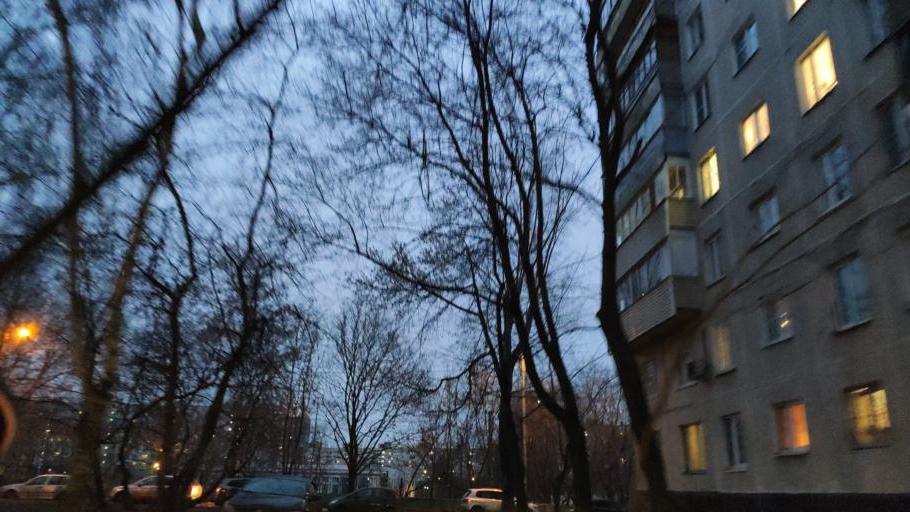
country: RU
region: Moscow
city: Lyublino
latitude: 55.6809
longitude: 37.7684
